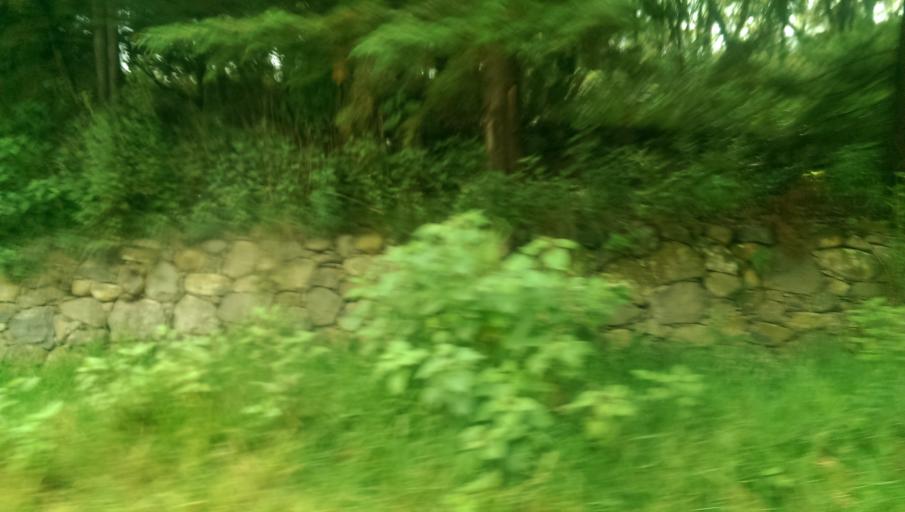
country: MX
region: Mexico
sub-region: Jilotepec
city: Jilotepec de Molina Enriquez
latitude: 19.9293
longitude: -99.4942
